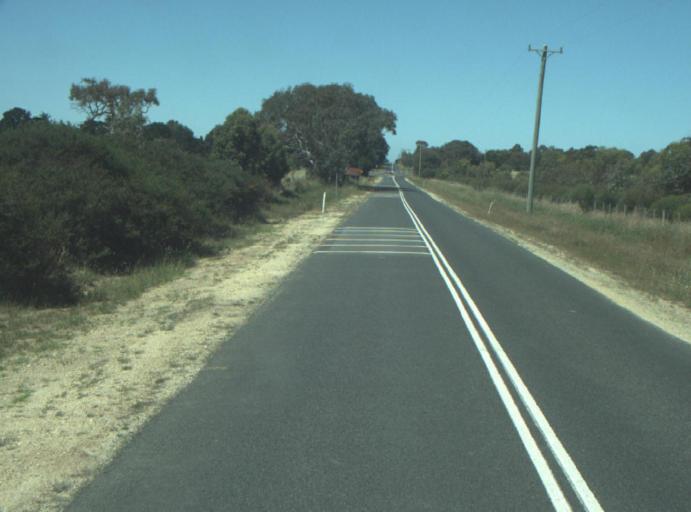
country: AU
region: Victoria
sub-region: Greater Geelong
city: Breakwater
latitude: -38.2470
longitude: 144.3515
